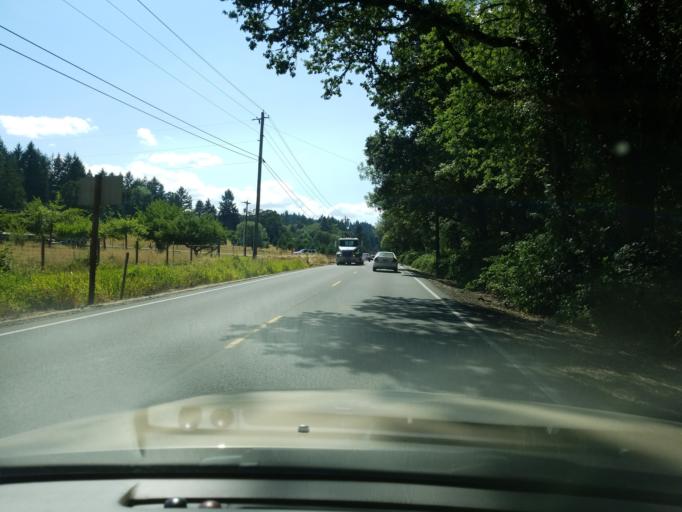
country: US
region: Oregon
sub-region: Yamhill County
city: Dundee
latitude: 45.3167
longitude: -123.0307
